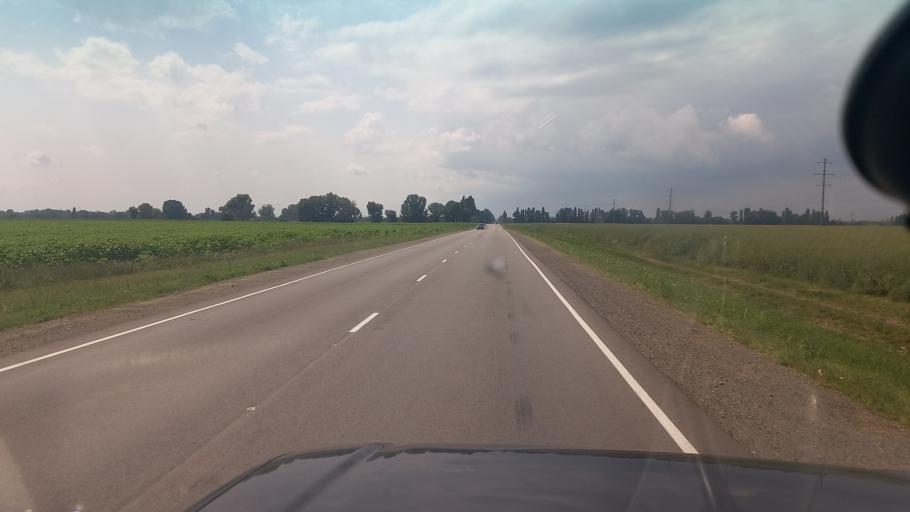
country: RU
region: Adygeya
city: Koshekhabl'
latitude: 44.9087
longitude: 40.4556
